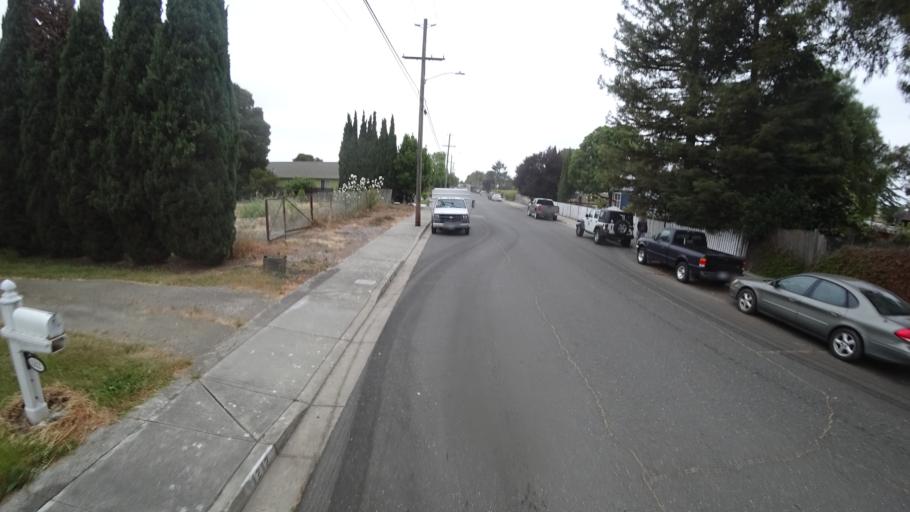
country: US
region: California
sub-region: Alameda County
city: Hayward
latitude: 37.6237
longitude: -122.0687
